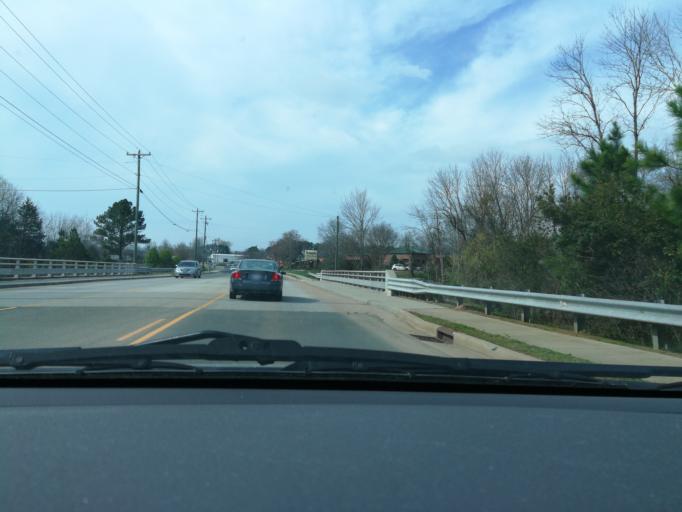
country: US
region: North Carolina
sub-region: Durham County
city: Durham
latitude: 35.9568
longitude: -78.9737
